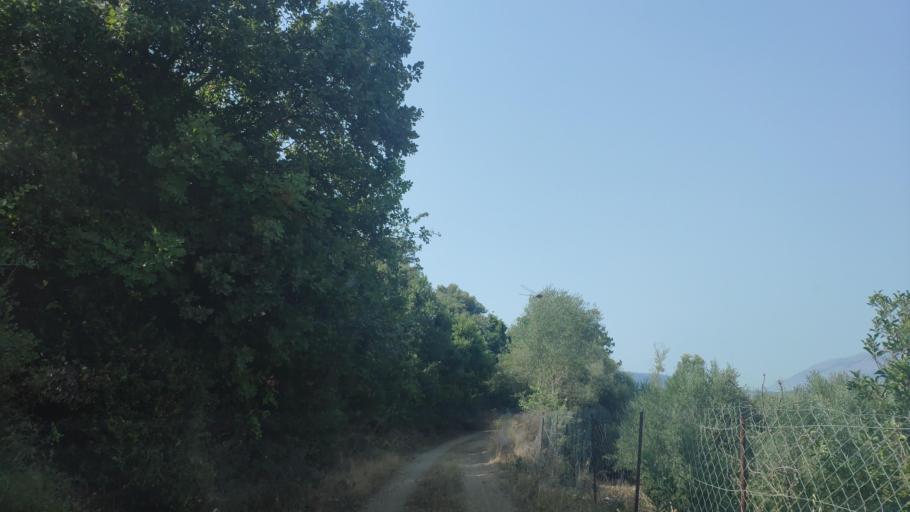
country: GR
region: West Greece
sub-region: Nomos Aitolias kai Akarnanias
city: Fitiai
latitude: 38.7310
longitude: 21.1839
